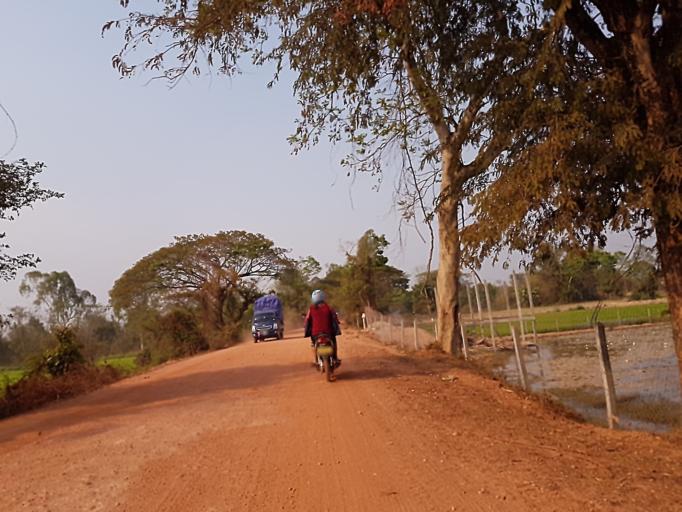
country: TH
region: Nong Khai
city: Phon Phisai
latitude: 18.0048
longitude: 102.9080
